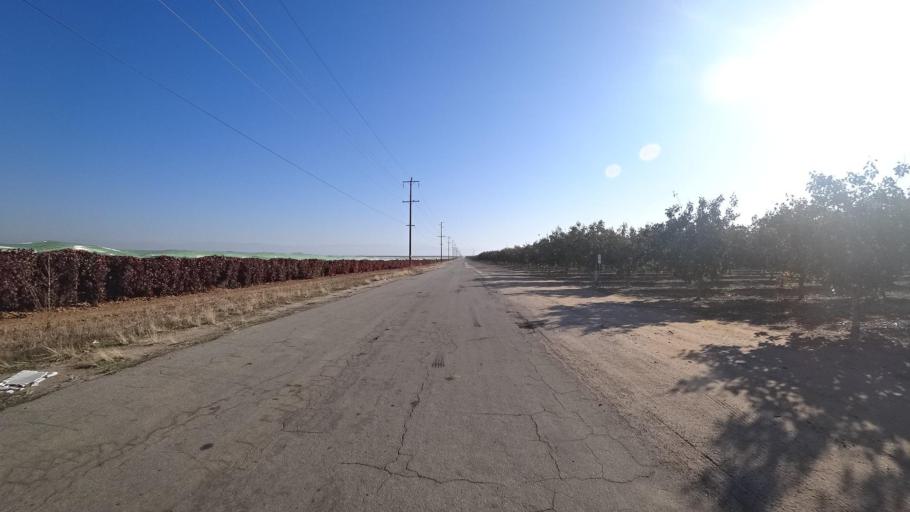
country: US
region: California
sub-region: Tulare County
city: Richgrove
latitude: 35.7326
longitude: -119.1249
